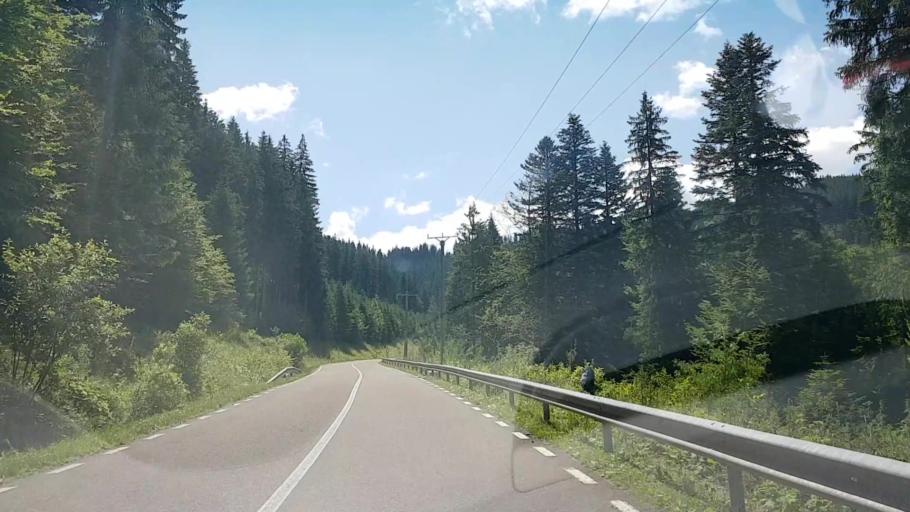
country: RO
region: Suceava
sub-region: Comuna Sadova
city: Sadova
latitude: 47.4695
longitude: 25.5131
